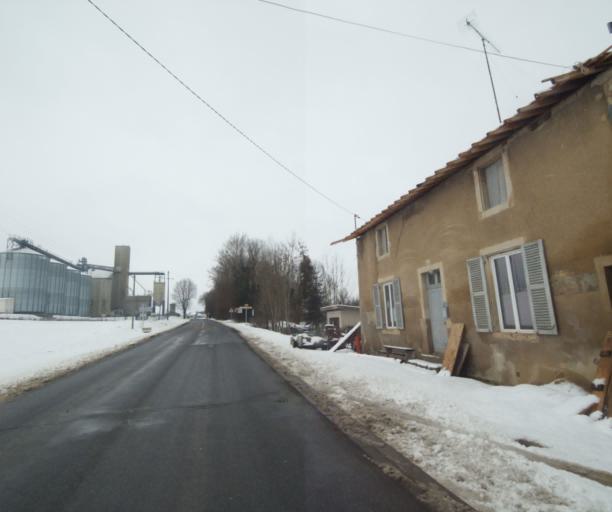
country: FR
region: Champagne-Ardenne
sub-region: Departement de la Haute-Marne
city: Wassy
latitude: 48.4355
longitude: 4.9610
